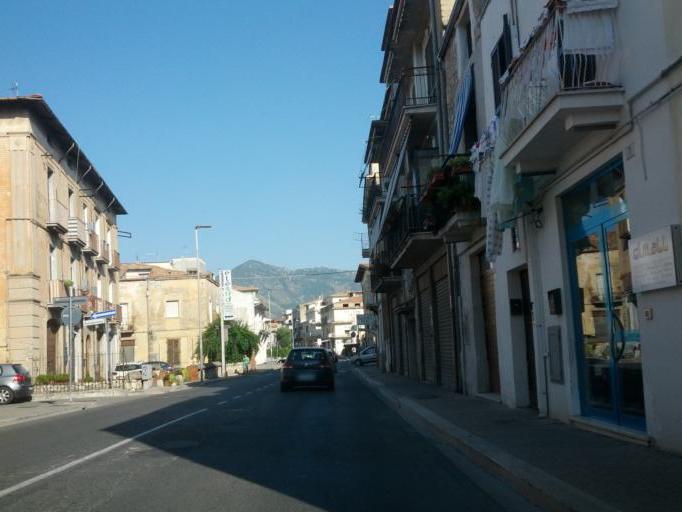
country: IT
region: Latium
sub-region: Provincia di Latina
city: Fondi
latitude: 41.3574
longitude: 13.4256
